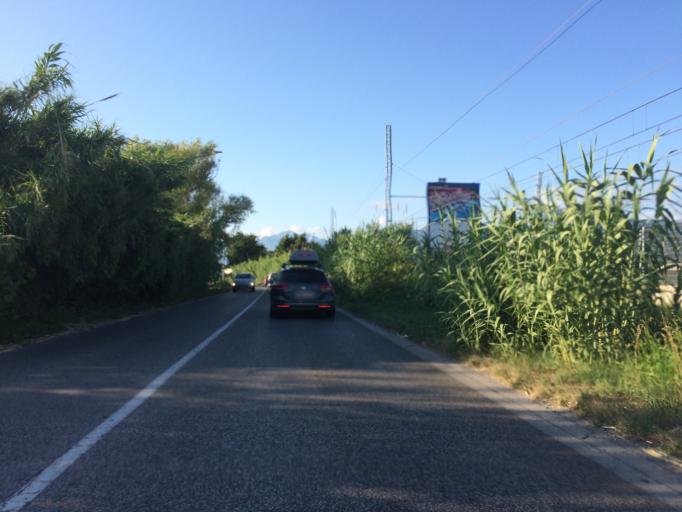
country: IT
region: Tuscany
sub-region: Provincia di Lucca
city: Viareggio
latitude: 43.8898
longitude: 10.2501
